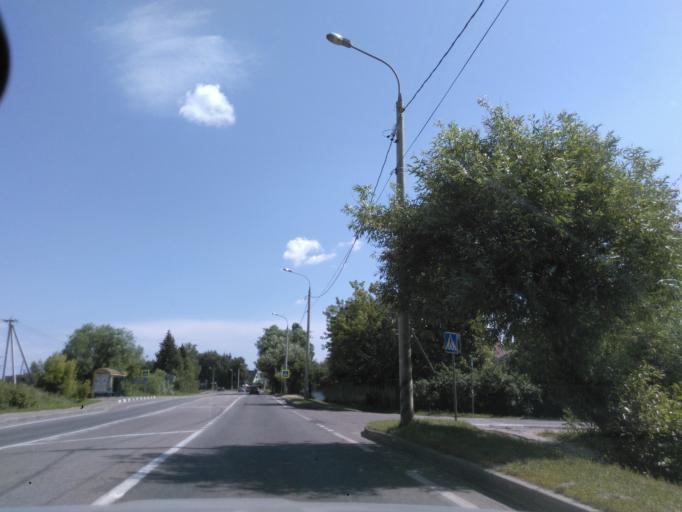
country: RU
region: Moskovskaya
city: Solnechnogorsk
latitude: 56.1808
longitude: 36.9567
